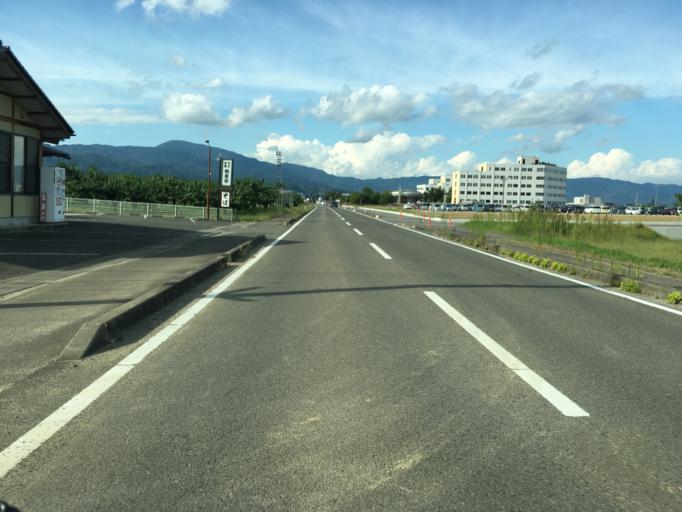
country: JP
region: Fukushima
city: Hobaramachi
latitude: 37.8149
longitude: 140.5206
